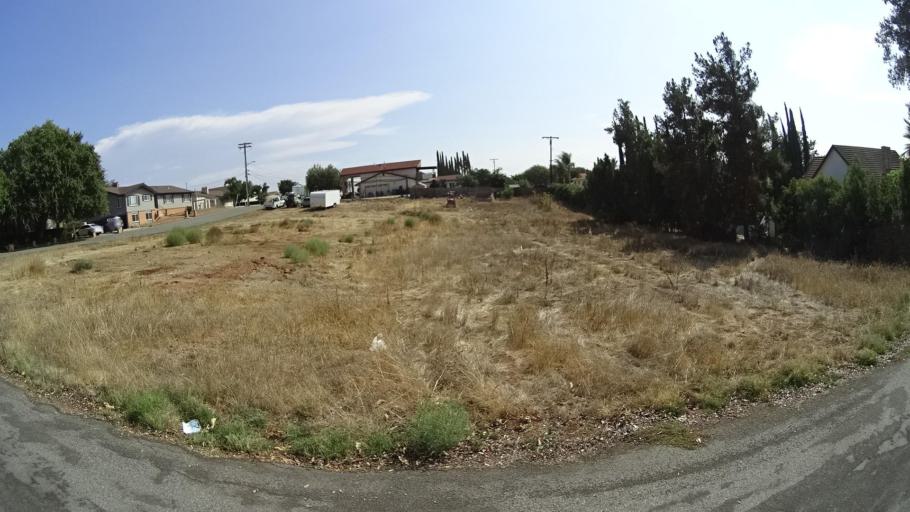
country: US
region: California
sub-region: San Diego County
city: Escondido
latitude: 33.1137
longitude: -117.0542
